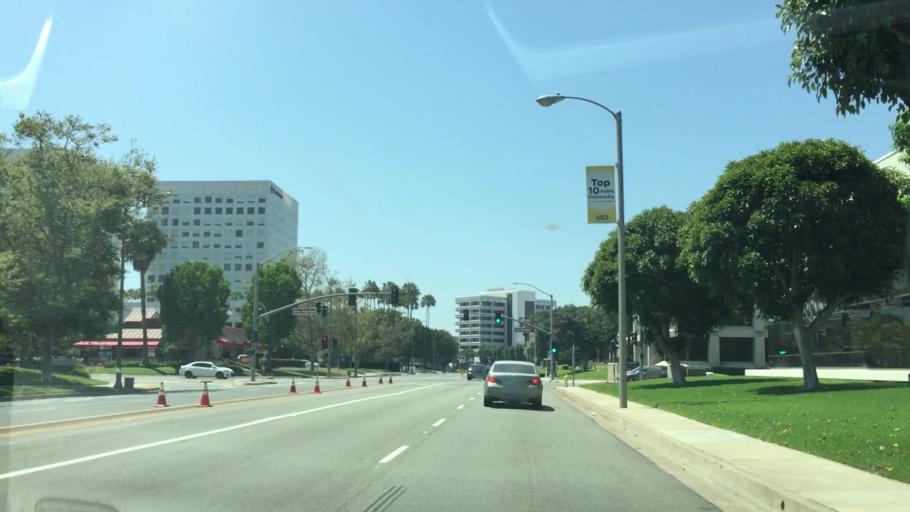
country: US
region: California
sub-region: Orange County
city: Irvine
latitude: 33.6692
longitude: -117.8586
